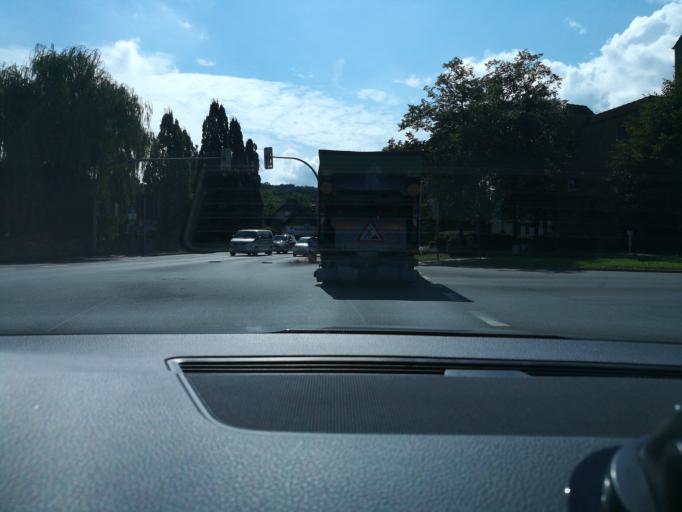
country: DE
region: North Rhine-Westphalia
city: Lubbecke
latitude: 52.3060
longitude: 8.6224
